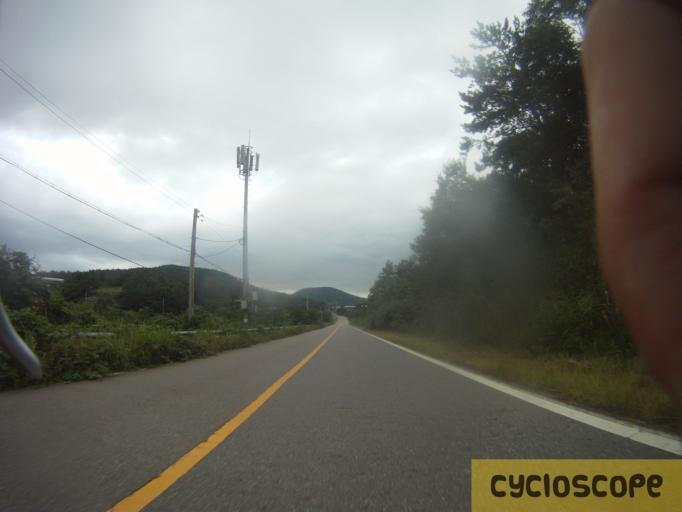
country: KR
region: Jeollanam-do
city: Beolgyo
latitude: 34.8474
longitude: 127.3509
